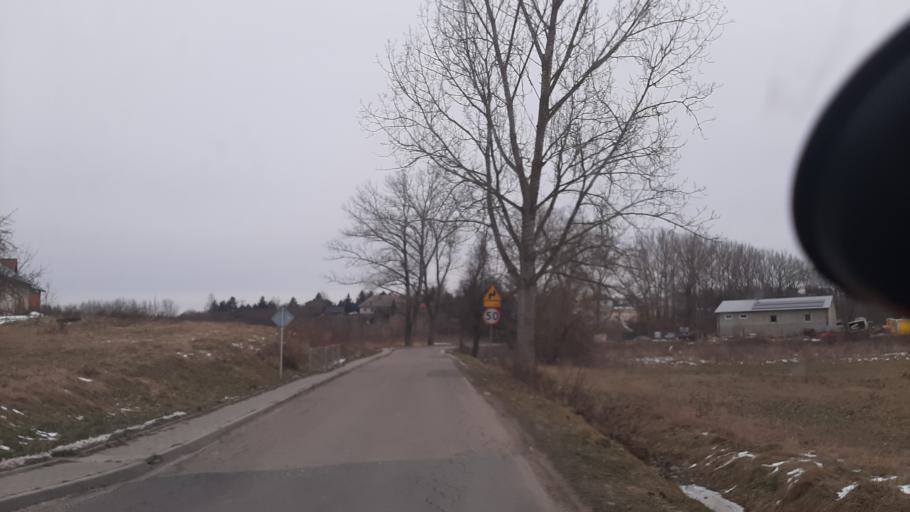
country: PL
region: Lublin Voivodeship
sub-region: Powiat lubelski
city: Jakubowice Murowane
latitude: 51.2811
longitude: 22.6041
